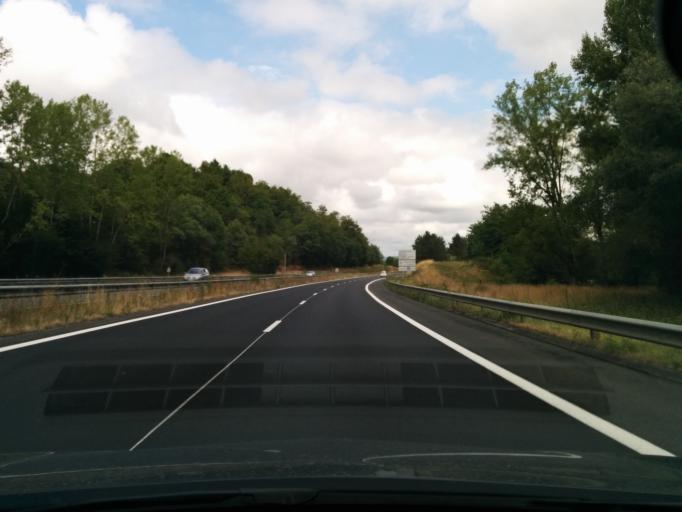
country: FR
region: Limousin
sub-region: Departement de la Correze
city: Brive-la-Gaillarde
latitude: 45.1298
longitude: 1.4924
